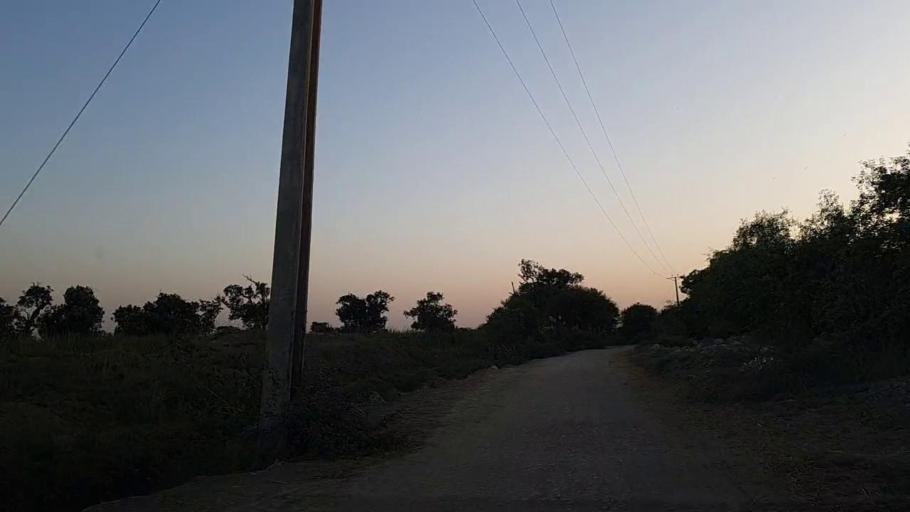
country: PK
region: Sindh
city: Mirpur Batoro
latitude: 24.6348
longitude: 68.1907
